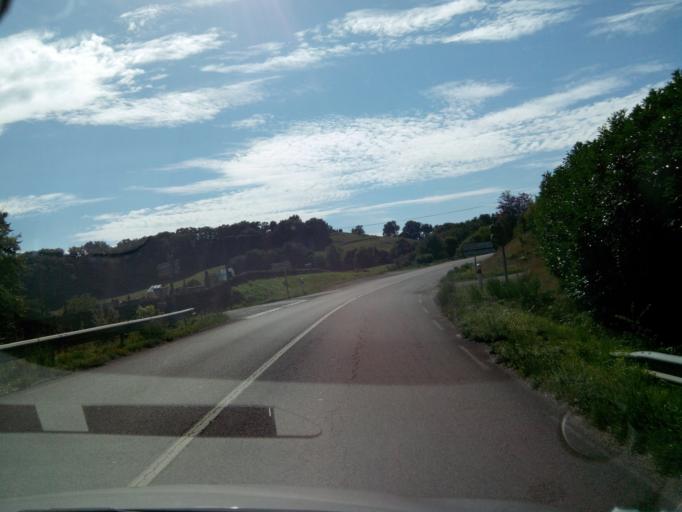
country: FR
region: Limousin
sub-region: Departement de la Correze
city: Meyssac
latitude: 45.0708
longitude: 1.6175
